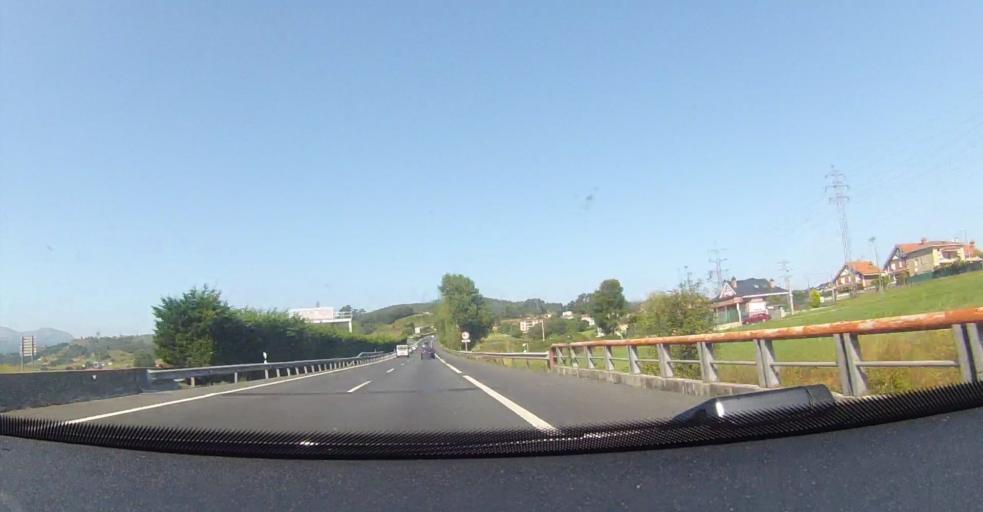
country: ES
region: Cantabria
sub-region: Provincia de Cantabria
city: Colindres
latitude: 43.3907
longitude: -3.4667
